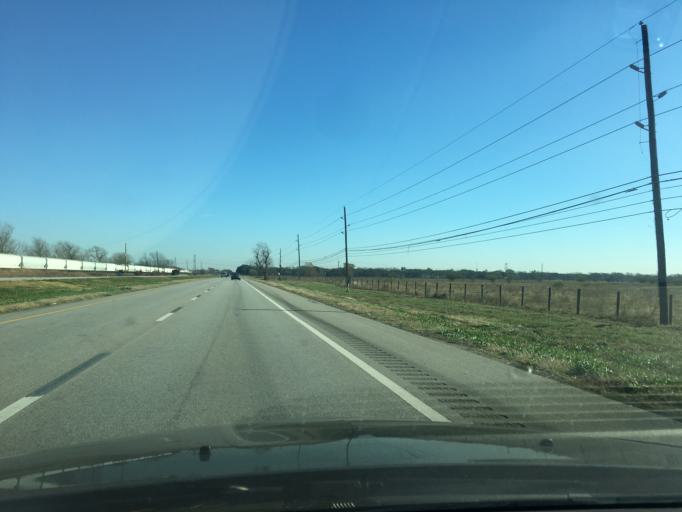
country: US
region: Texas
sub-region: Fort Bend County
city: New Territory
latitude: 29.5993
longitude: -95.7063
